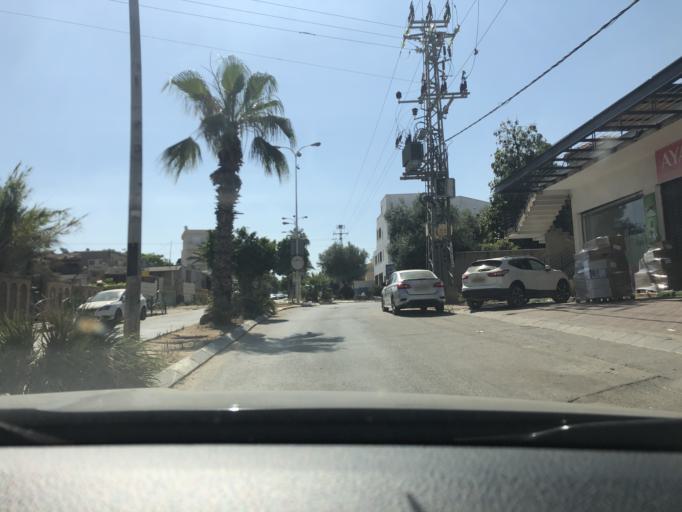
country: IL
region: Central District
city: Jaljulya
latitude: 32.1526
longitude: 34.9562
